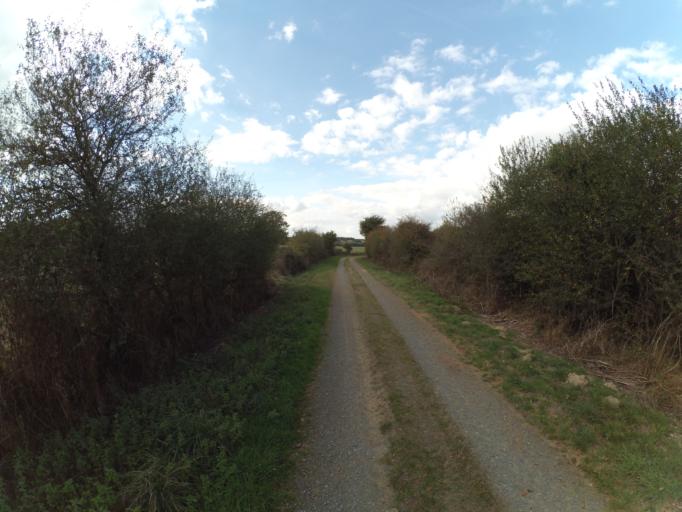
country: FR
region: Pays de la Loire
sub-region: Departement de la Loire-Atlantique
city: Saint-Lumine-de-Clisson
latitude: 47.0728
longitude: -1.3310
